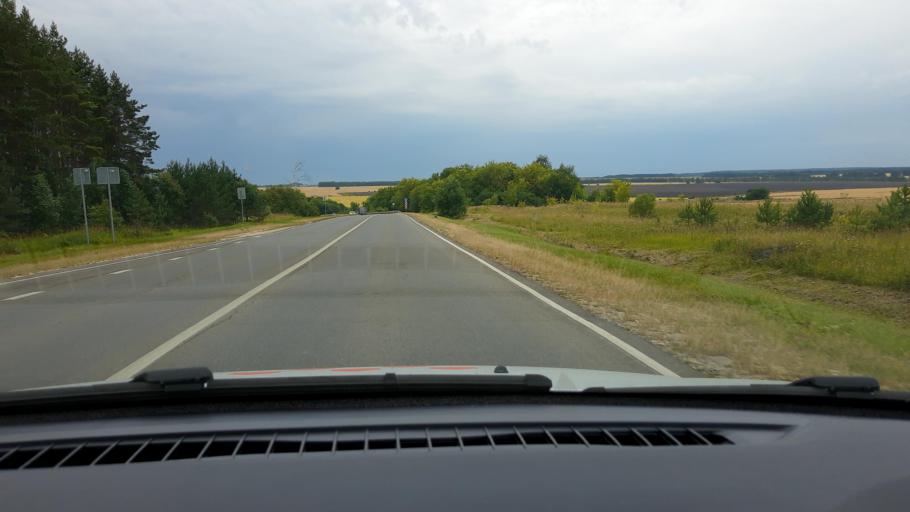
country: RU
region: Nizjnij Novgorod
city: Vyyezdnoye
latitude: 55.1483
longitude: 43.5662
